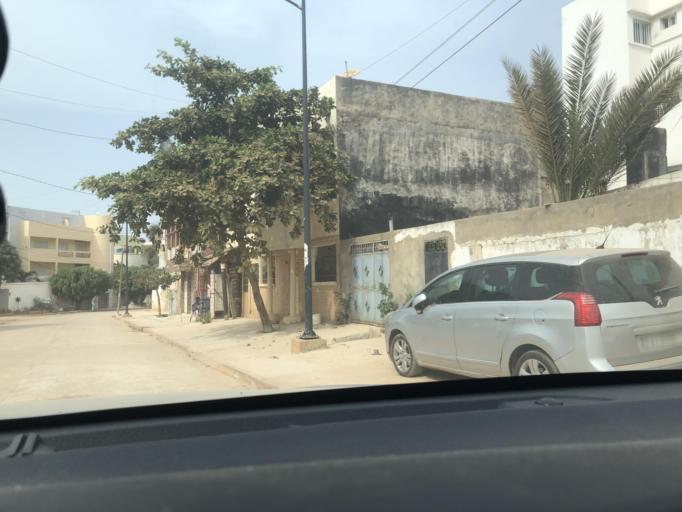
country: SN
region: Dakar
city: Mermoz Boabab
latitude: 14.7298
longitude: -17.4979
